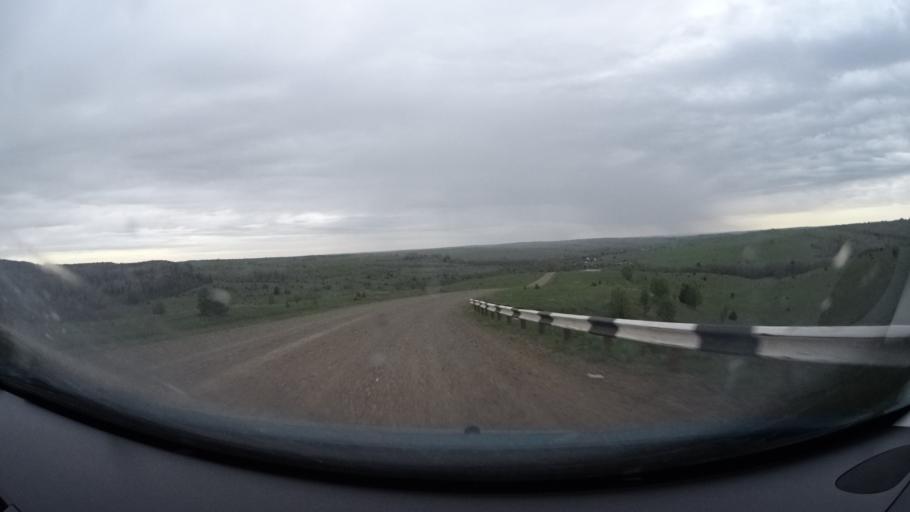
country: RU
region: Perm
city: Kuyeda
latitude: 56.5676
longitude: 55.6836
